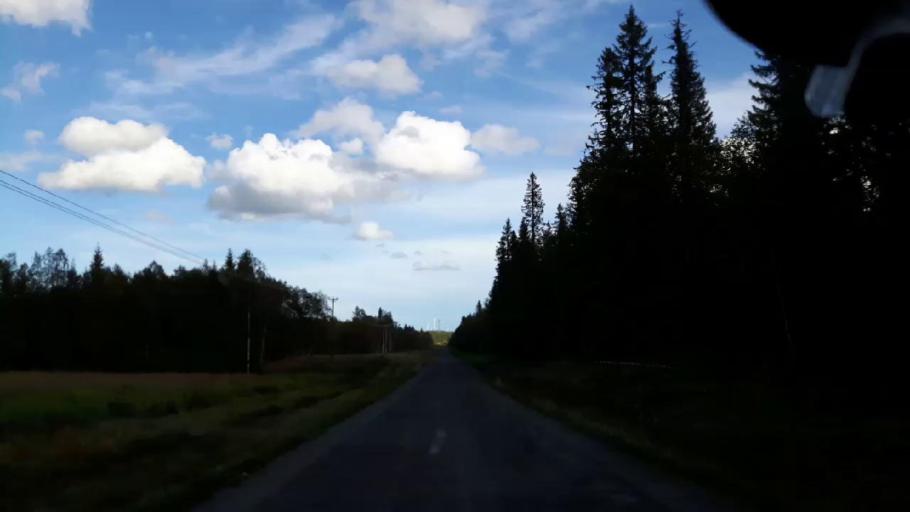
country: SE
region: Jaemtland
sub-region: Ragunda Kommun
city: Hammarstrand
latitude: 63.4381
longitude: 16.0028
